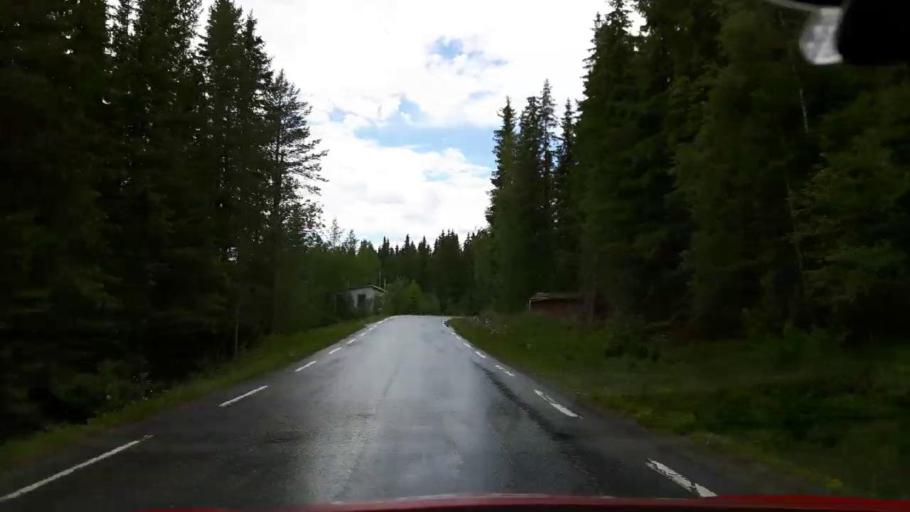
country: NO
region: Nord-Trondelag
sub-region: Lierne
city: Sandvika
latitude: 64.0925
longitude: 14.0498
